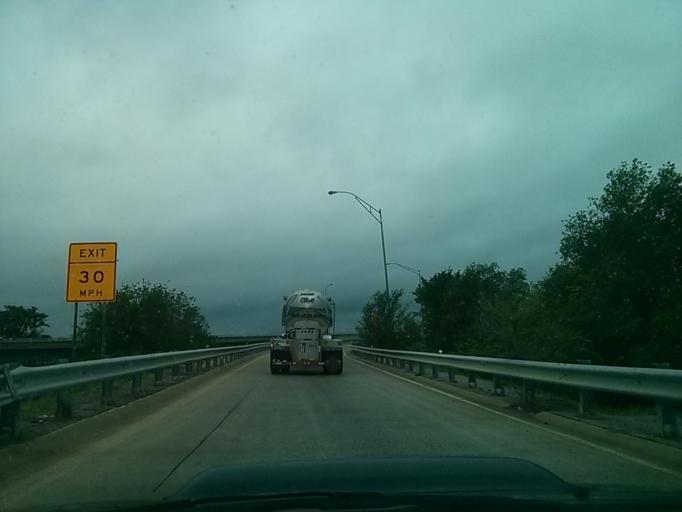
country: US
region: Oklahoma
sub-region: Tulsa County
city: Tulsa
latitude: 36.1525
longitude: -95.9992
